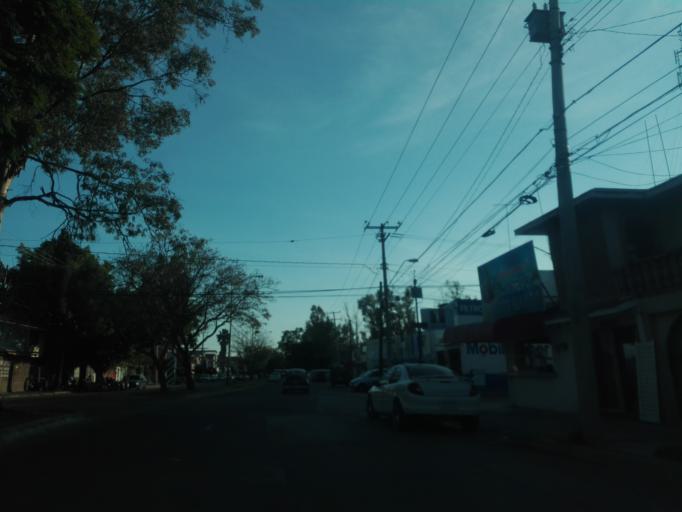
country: MX
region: Guanajuato
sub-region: Leon
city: San Jose de Duran (Los Troncoso)
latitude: 21.0941
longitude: -101.6472
